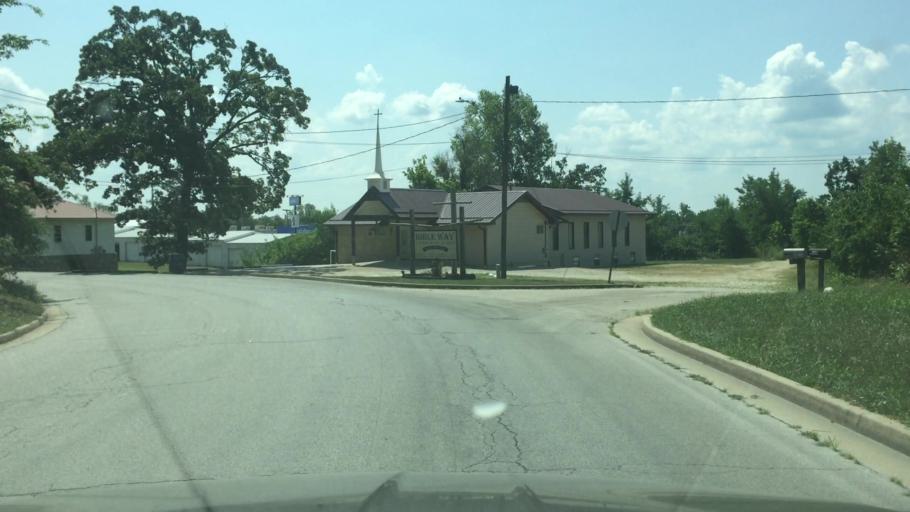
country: US
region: Missouri
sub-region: Miller County
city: Eldon
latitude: 38.3374
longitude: -92.5864
